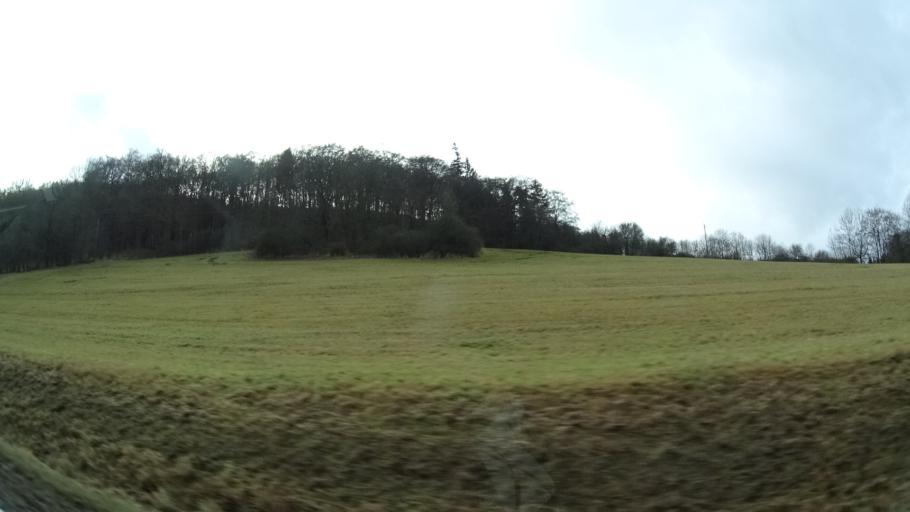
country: DE
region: Thuringia
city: Aschenhausen
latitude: 50.6064
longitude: 10.1954
